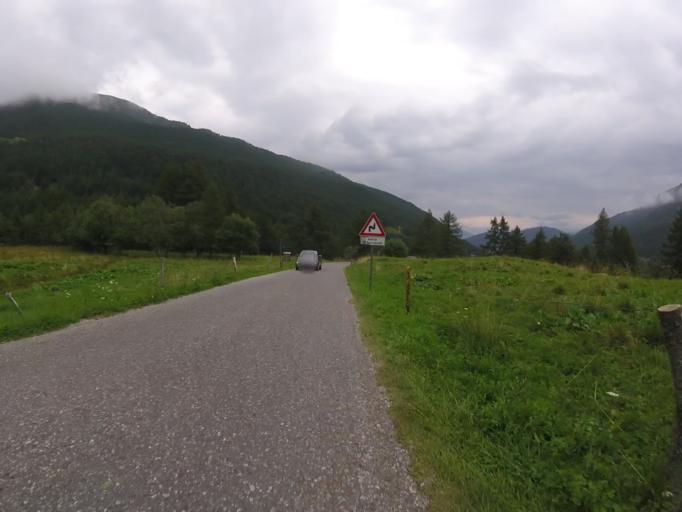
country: IT
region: Lombardy
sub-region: Provincia di Brescia
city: Monno
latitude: 46.2459
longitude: 10.3178
